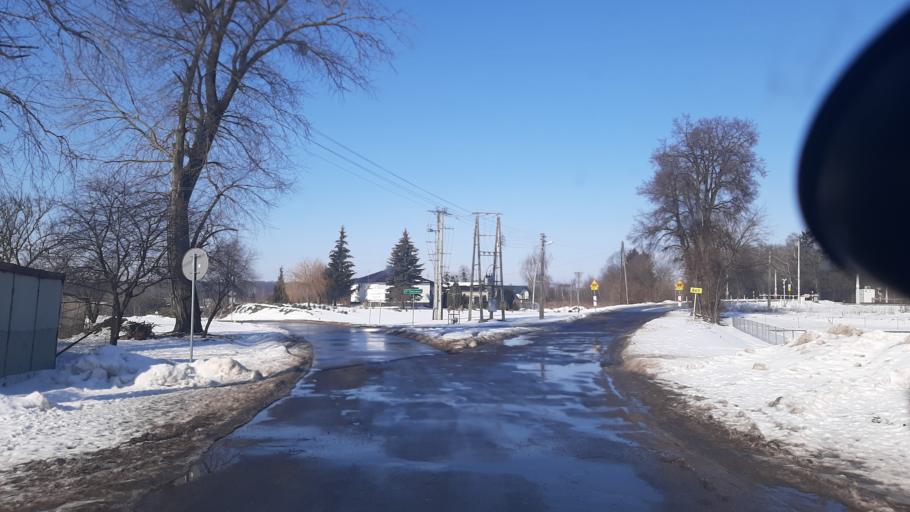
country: PL
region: Lublin Voivodeship
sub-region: Powiat lubelski
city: Wojciechow
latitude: 51.2879
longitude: 22.2805
